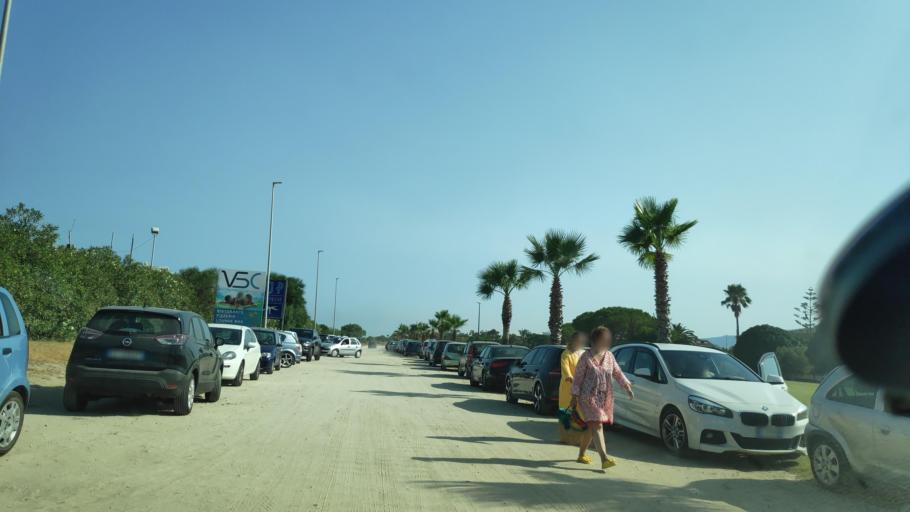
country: IT
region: Calabria
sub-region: Provincia di Catanzaro
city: Isca Marina
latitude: 38.6034
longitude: 16.5657
